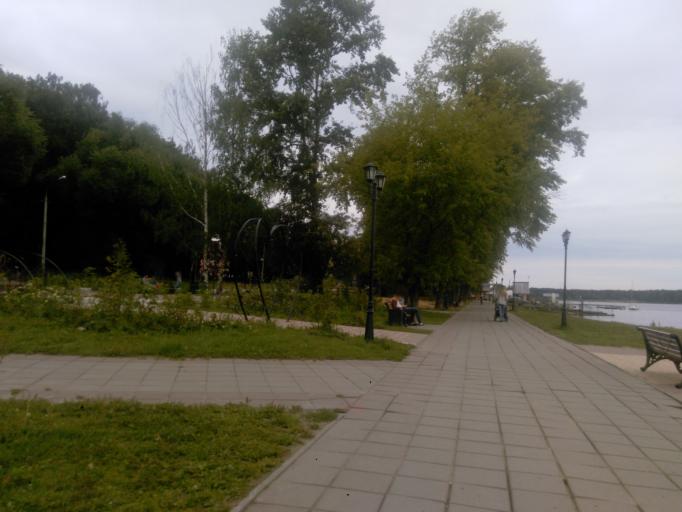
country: RU
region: Moskovskaya
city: Solnechnogorsk
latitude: 56.1930
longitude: 36.9841
